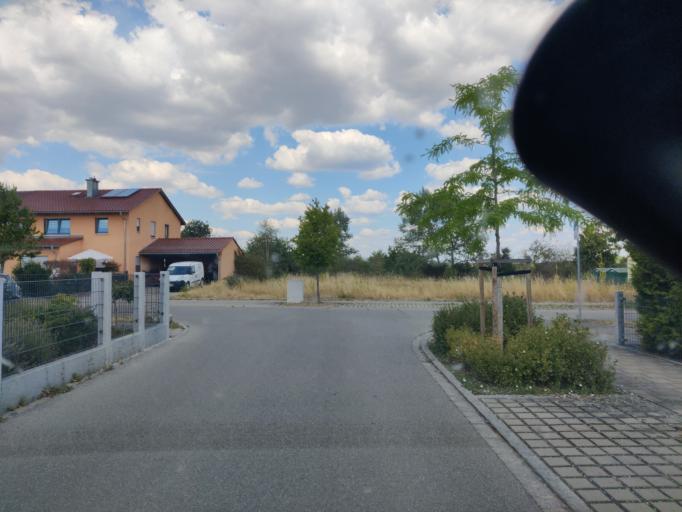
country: DE
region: Bavaria
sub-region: Regierungsbezirk Mittelfranken
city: Hilpoltstein
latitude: 49.1965
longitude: 11.1857
